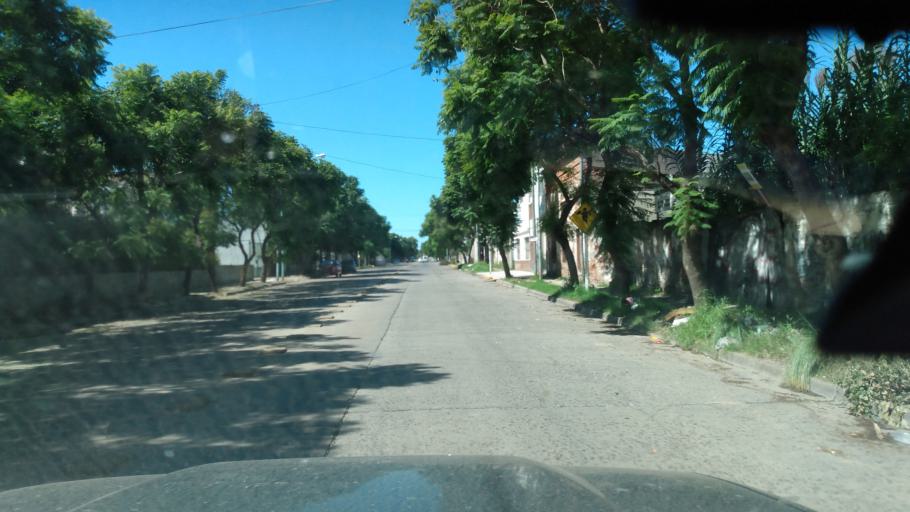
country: AR
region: Buenos Aires
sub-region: Partido de Lujan
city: Lujan
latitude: -34.5699
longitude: -59.1183
